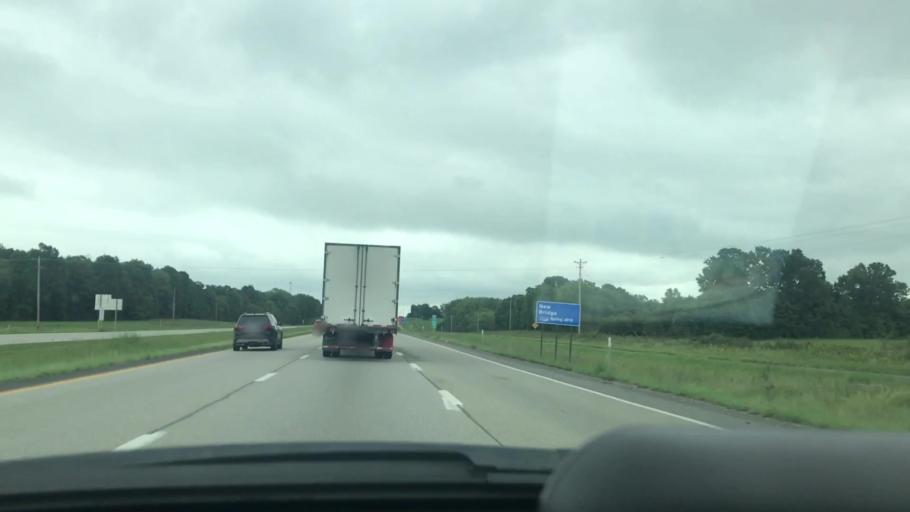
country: US
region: Missouri
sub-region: Greene County
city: Republic
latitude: 37.1858
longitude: -93.5665
